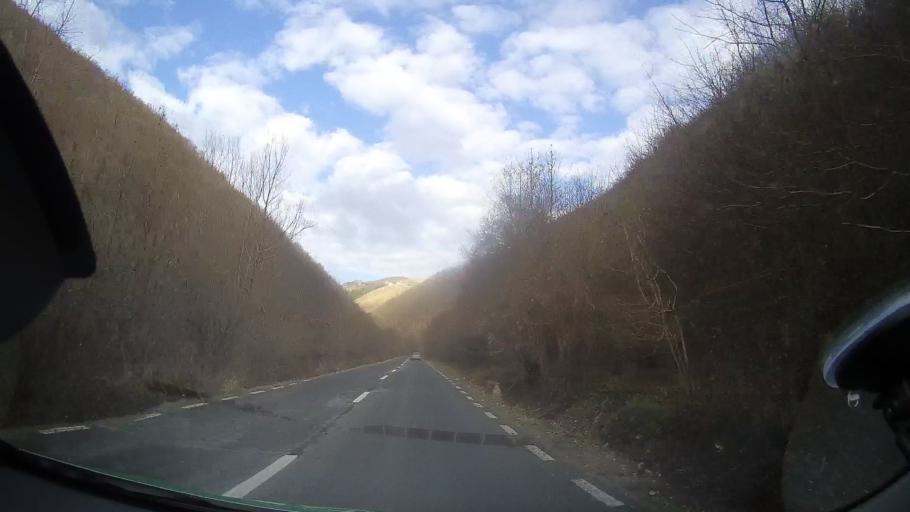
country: RO
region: Cluj
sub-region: Comuna Baisoara
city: Baisoara
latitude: 46.5871
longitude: 23.4422
